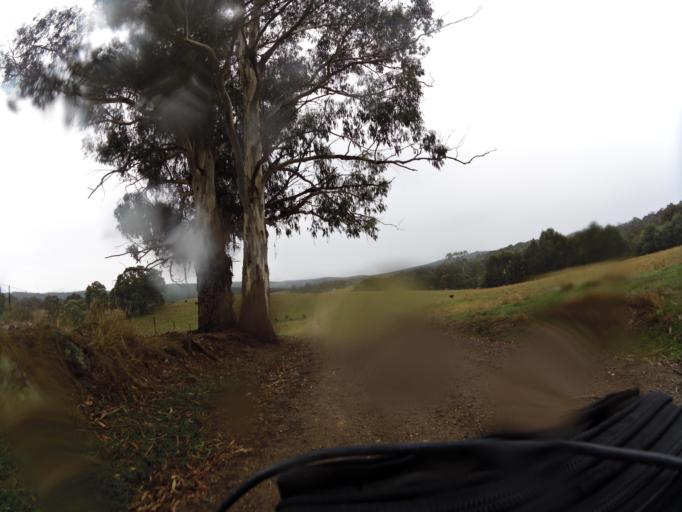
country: AU
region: New South Wales
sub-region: Greater Hume Shire
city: Holbrook
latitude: -36.1597
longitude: 147.4897
